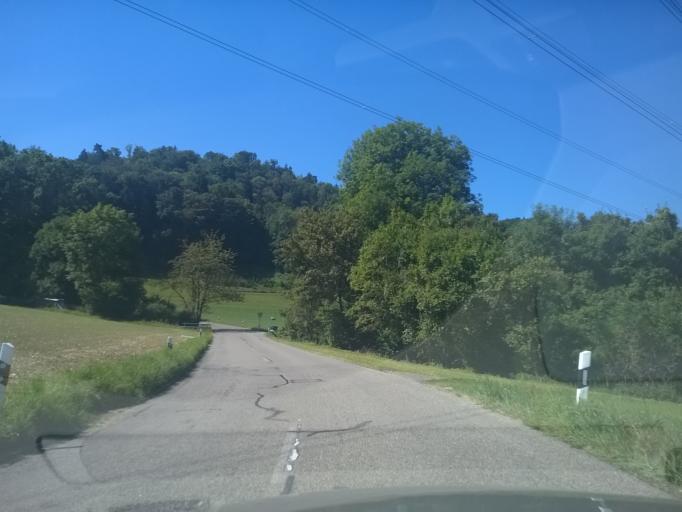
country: CH
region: Zurich
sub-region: Bezirk Winterthur
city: Pfungen
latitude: 47.5127
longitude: 8.6335
